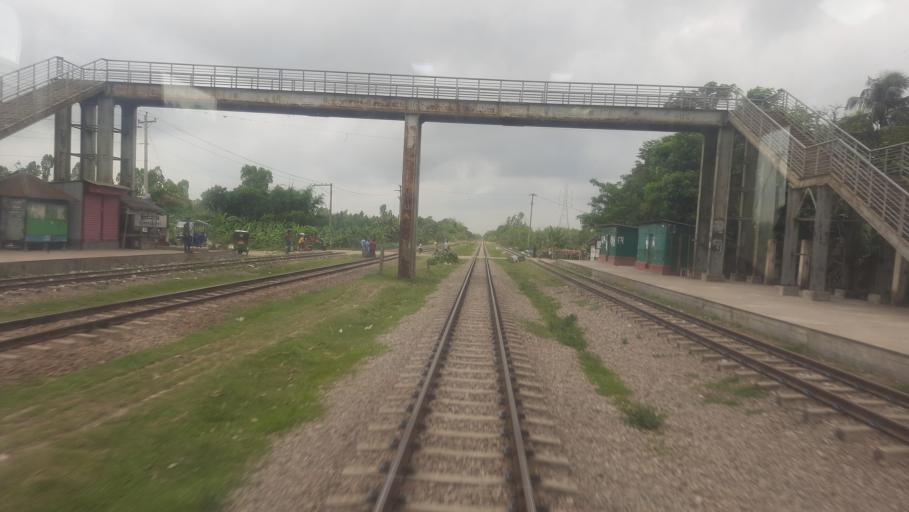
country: BD
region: Dhaka
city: Bhairab Bazar
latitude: 24.0057
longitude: 90.9021
